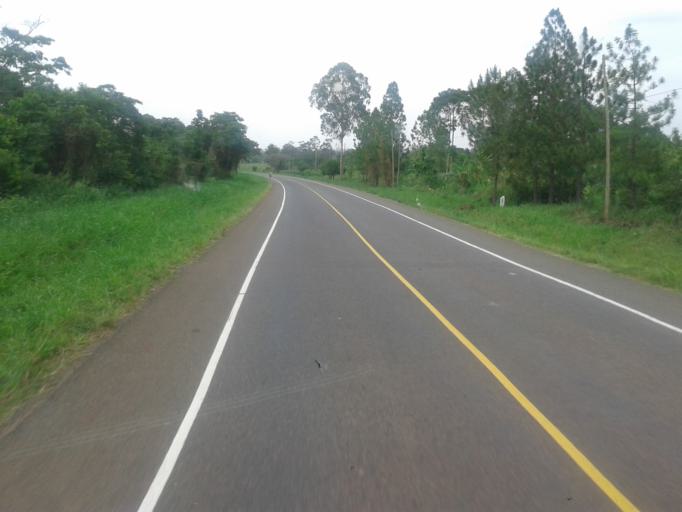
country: UG
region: Northern Region
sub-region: Oyam District
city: Oyam
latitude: 2.1495
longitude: 32.2127
